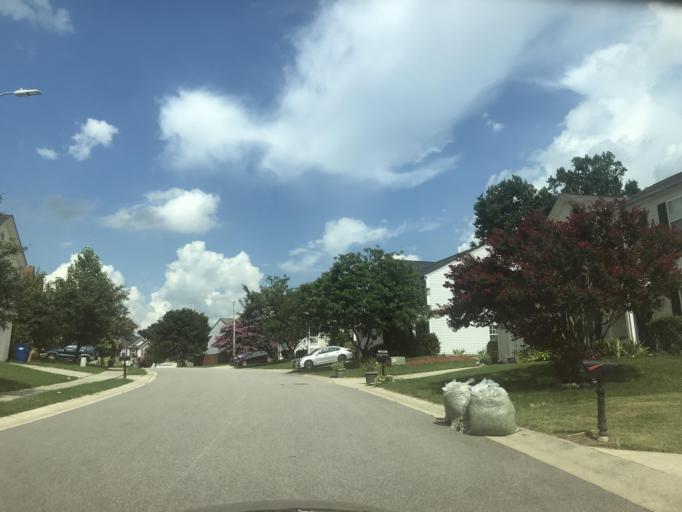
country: US
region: North Carolina
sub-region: Wake County
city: Knightdale
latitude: 35.8392
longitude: -78.5592
